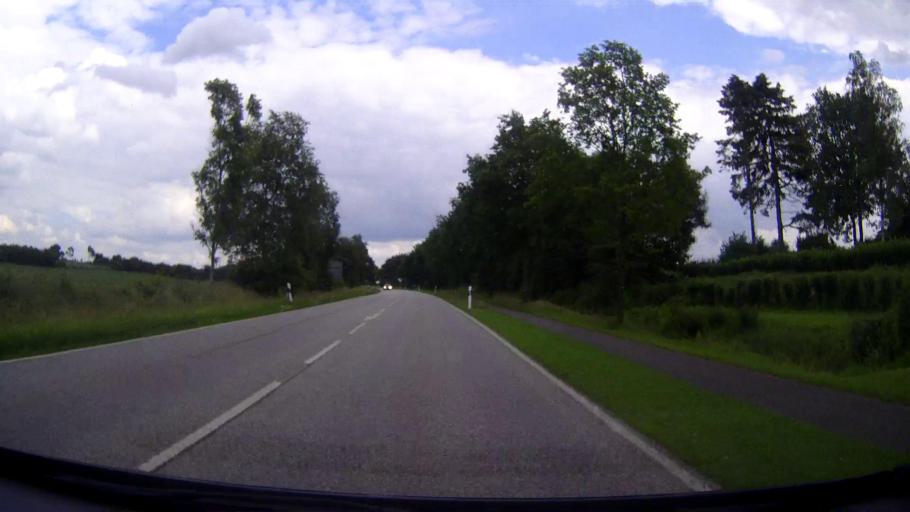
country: DE
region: Schleswig-Holstein
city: Beldorf
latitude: 54.1211
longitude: 9.3442
